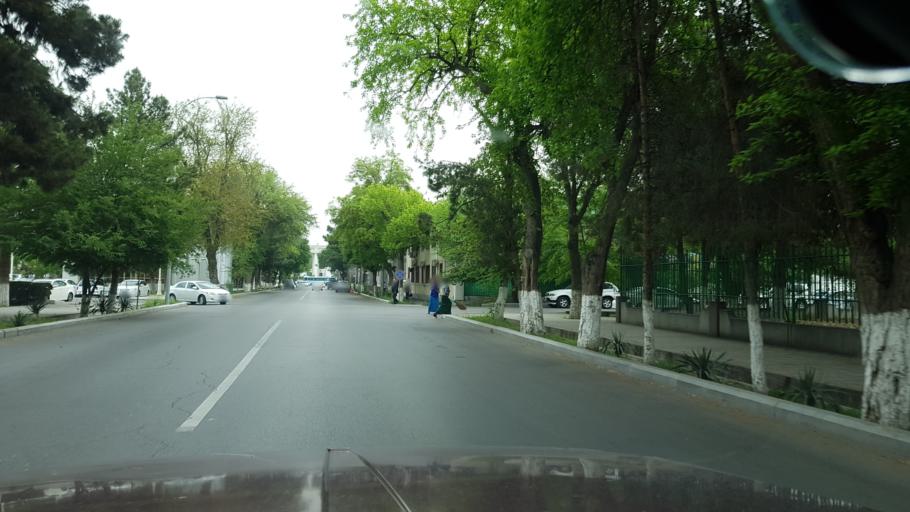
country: TM
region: Ahal
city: Ashgabat
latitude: 37.9403
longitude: 58.3867
